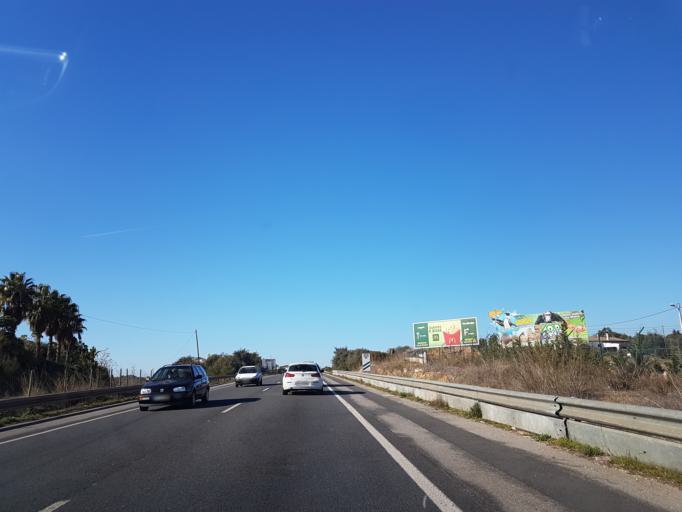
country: PT
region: Faro
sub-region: Portimao
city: Portimao
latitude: 37.1547
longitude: -8.5306
